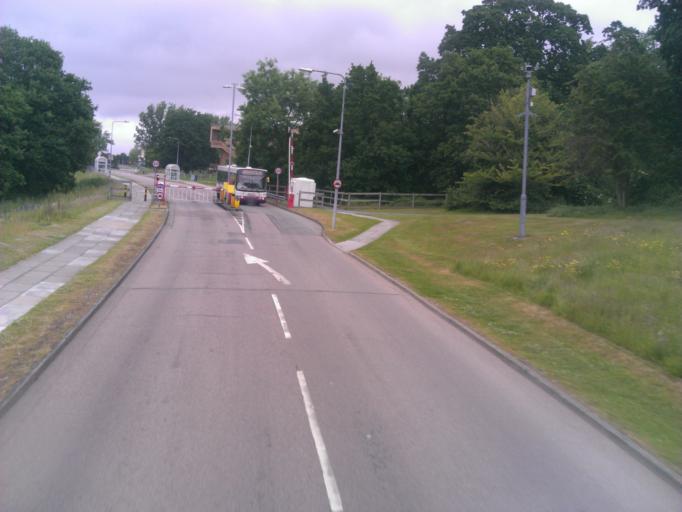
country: GB
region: England
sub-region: Essex
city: Rowhedge
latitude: 51.8768
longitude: 0.9421
